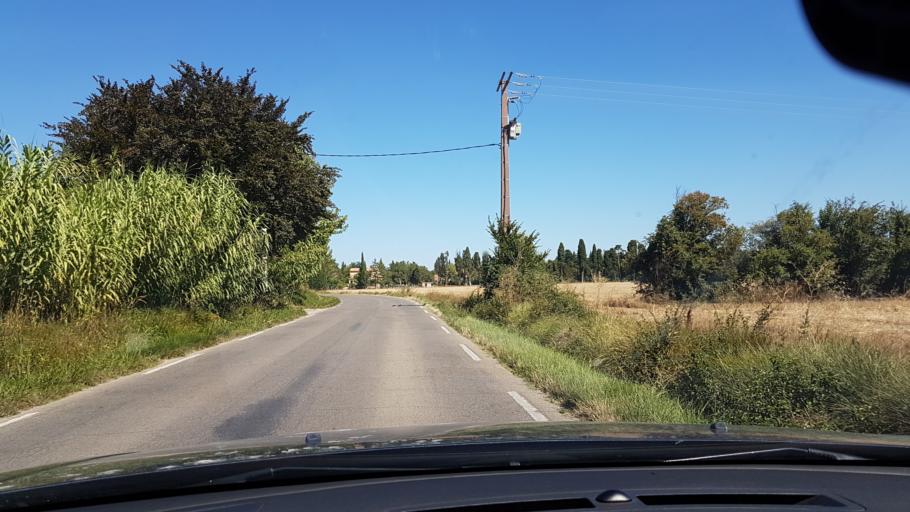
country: FR
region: Provence-Alpes-Cote d'Azur
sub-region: Departement des Bouches-du-Rhone
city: Molleges
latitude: 43.7986
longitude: 4.9529
